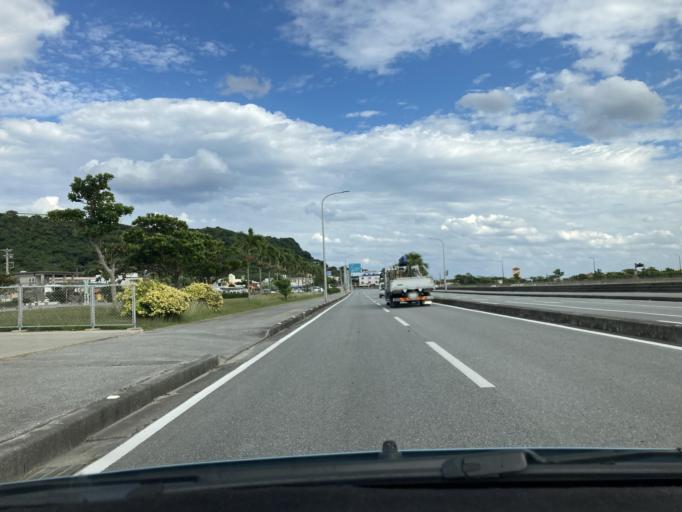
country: JP
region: Okinawa
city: Katsuren-haebaru
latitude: 26.3403
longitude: 127.9522
